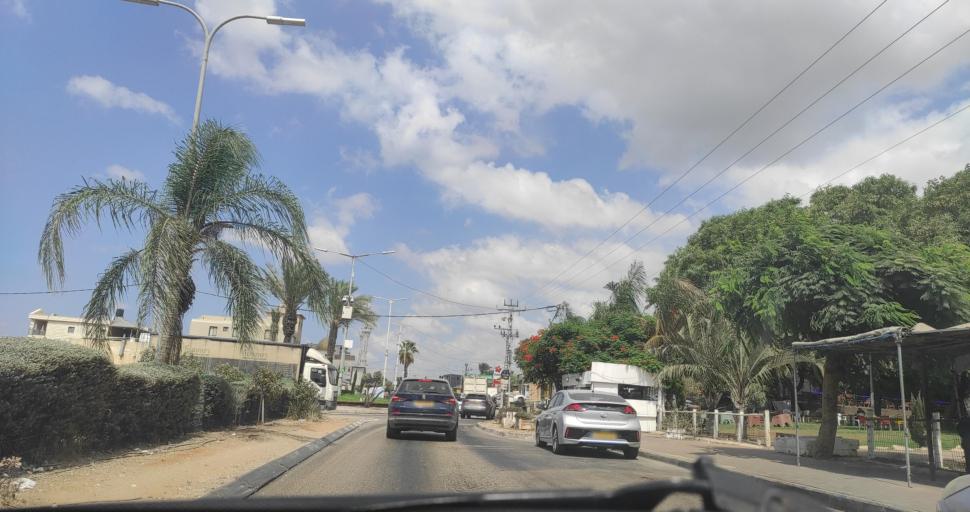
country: IL
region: Central District
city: Kafr Qasim
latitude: 32.1122
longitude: 34.9637
